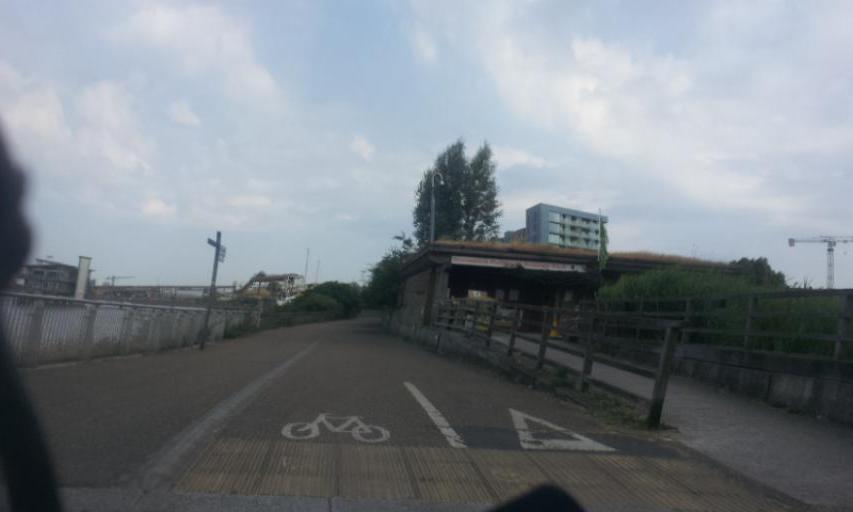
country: GB
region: England
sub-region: Greater London
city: Blackheath
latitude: 51.4960
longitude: 0.0154
